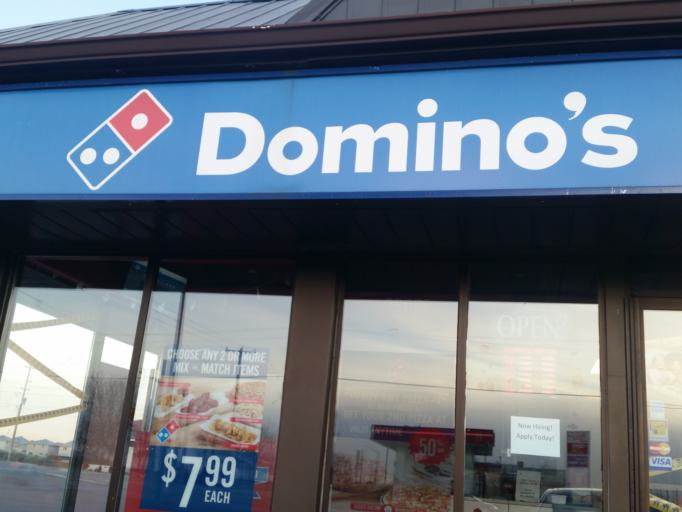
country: CA
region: Ontario
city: Arnprior
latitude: 45.4236
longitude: -76.3692
